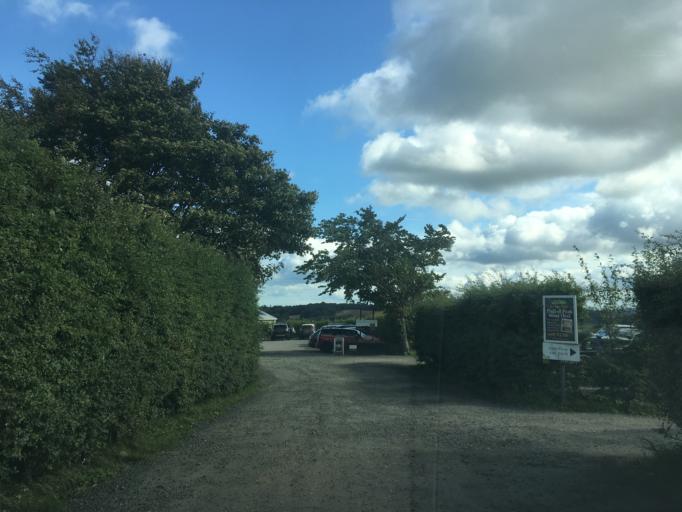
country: GB
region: Scotland
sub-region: Edinburgh
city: Queensferry
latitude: 55.9724
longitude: -3.3523
